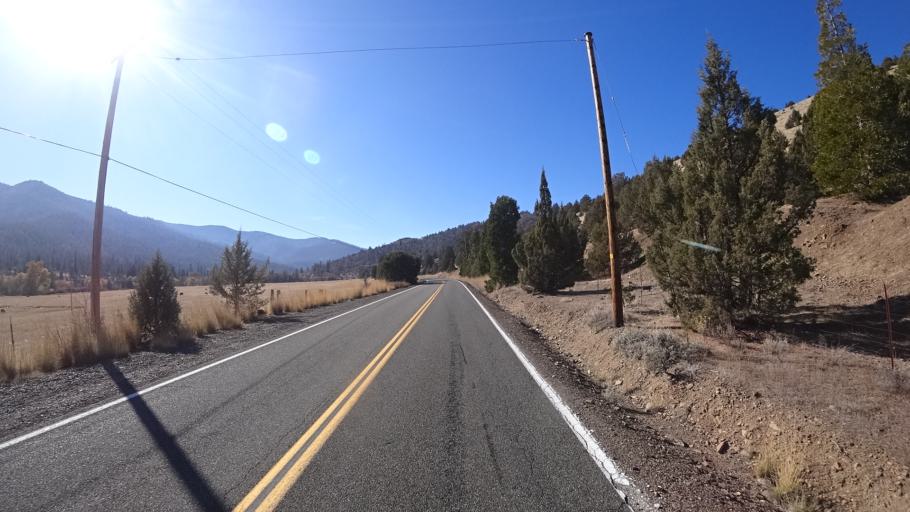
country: US
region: California
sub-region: Siskiyou County
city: Weed
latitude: 41.4867
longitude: -122.5681
